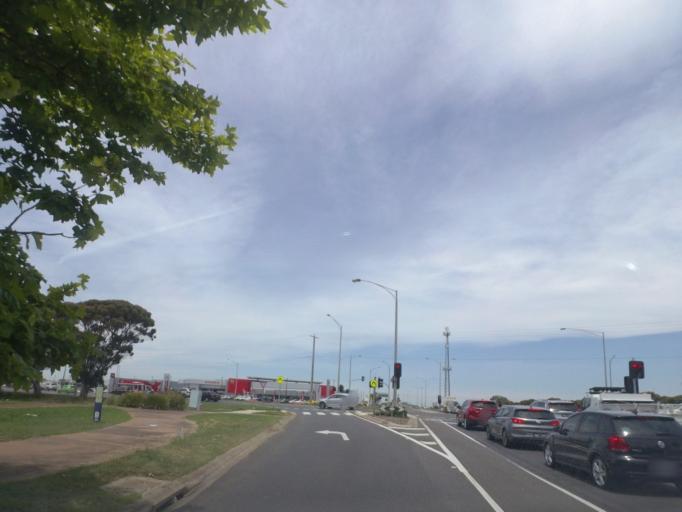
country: AU
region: Victoria
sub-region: Melton
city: Caroline Springs
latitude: -37.7556
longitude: 144.7399
